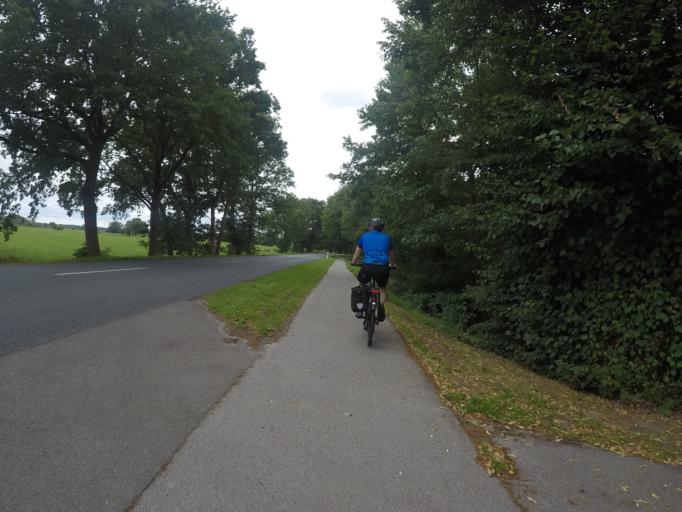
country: DE
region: Lower Saxony
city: Himmelpforten
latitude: 53.6331
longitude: 9.3010
